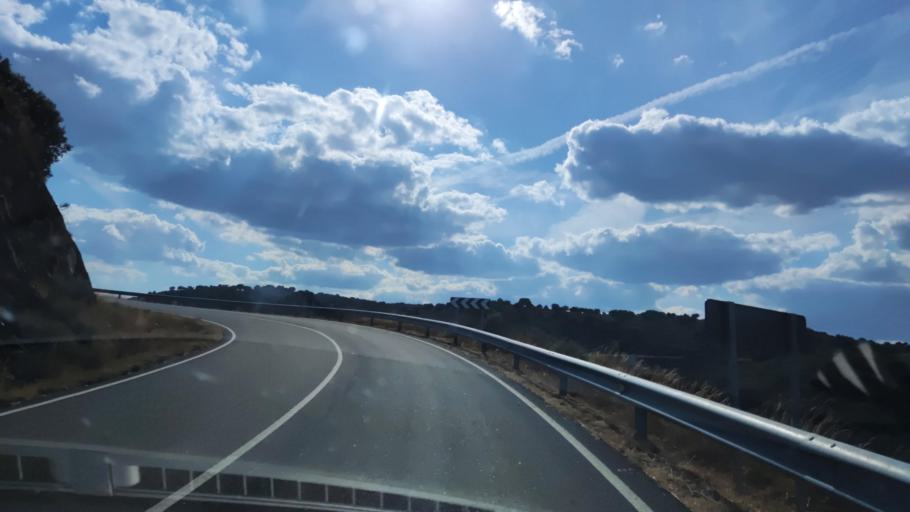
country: ES
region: Castille and Leon
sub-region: Provincia de Salamanca
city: Pastores
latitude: 40.4972
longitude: -6.4942
